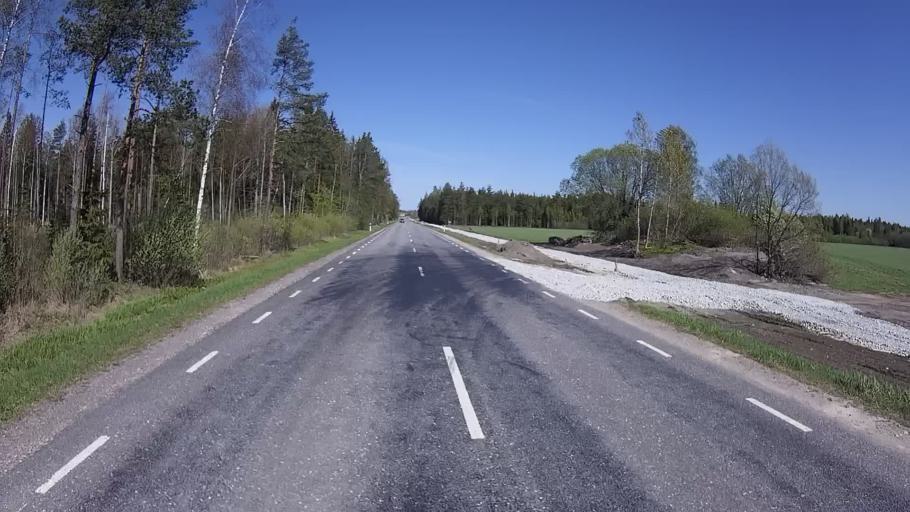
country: EE
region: Paernumaa
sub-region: Tootsi vald
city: Tootsi
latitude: 58.4927
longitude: 24.8073
